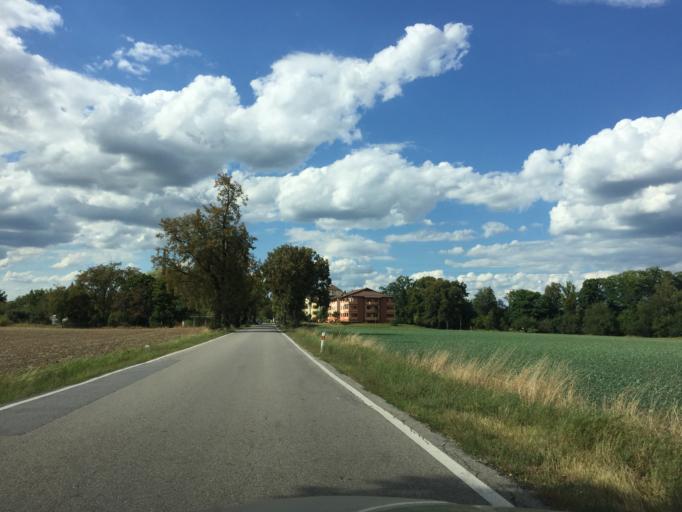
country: CZ
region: Jihocesky
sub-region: Okres Ceske Budejovice
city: Ceske Budejovice
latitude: 48.9527
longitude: 14.4811
